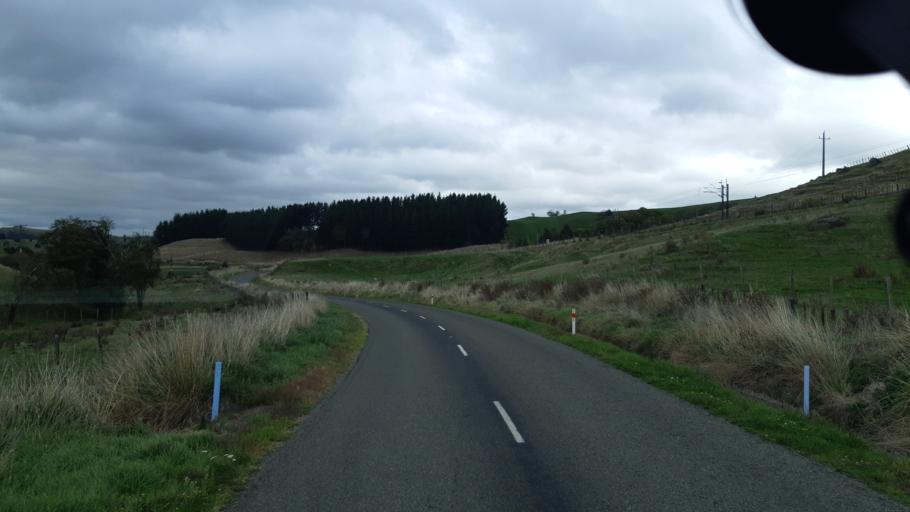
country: NZ
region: Manawatu-Wanganui
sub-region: Ruapehu District
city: Waiouru
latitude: -39.6514
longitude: 175.7525
